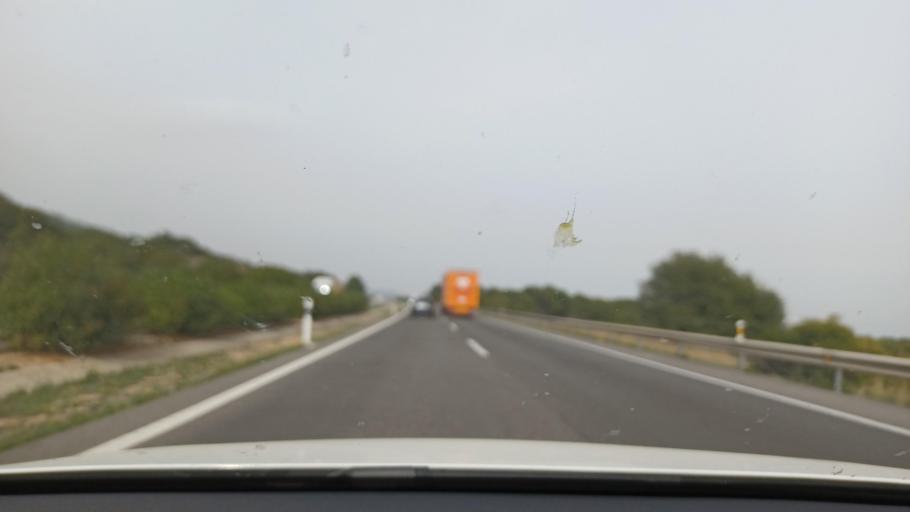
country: ES
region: Valencia
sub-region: Provincia de Castello
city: Benicassim
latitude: 40.0372
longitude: 0.0147
